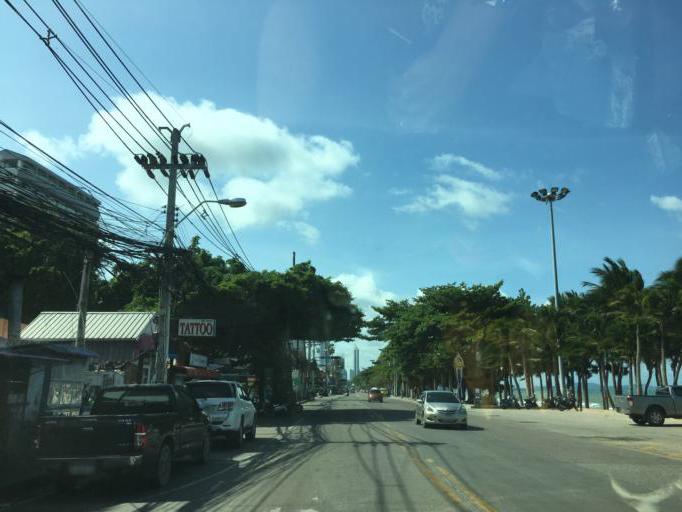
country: TH
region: Chon Buri
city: Phatthaya
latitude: 12.8867
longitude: 100.8777
